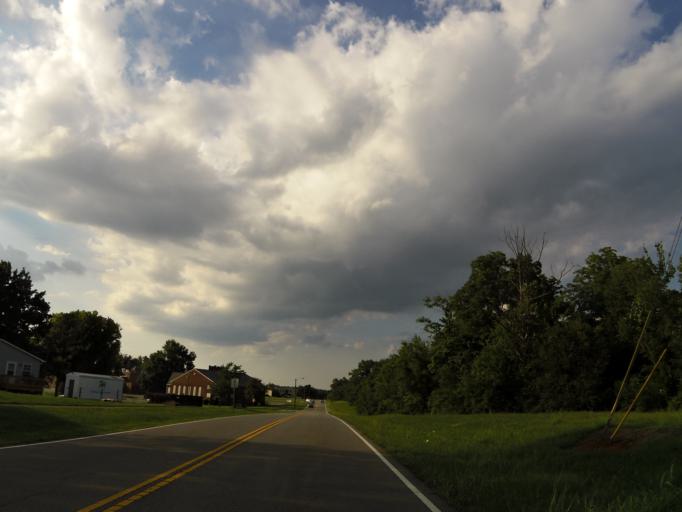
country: US
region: Tennessee
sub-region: Blount County
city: Alcoa
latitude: 35.7778
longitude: -83.9773
